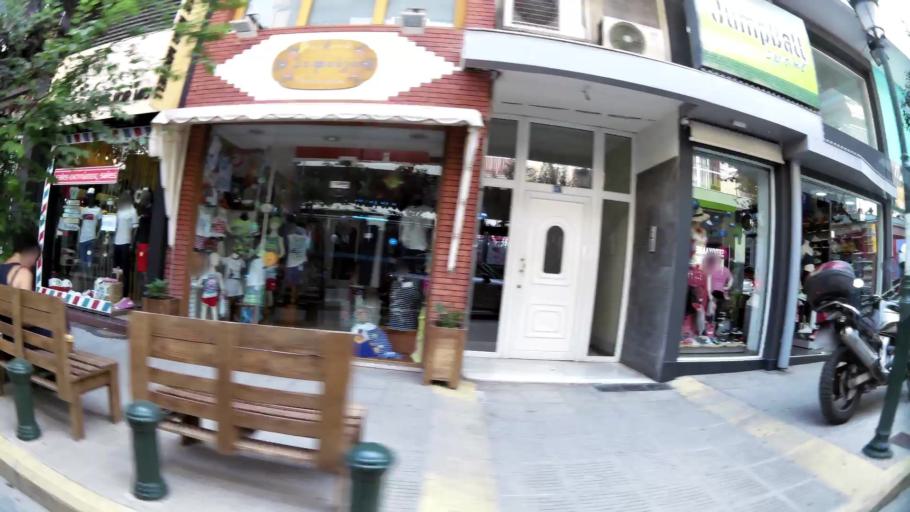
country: GR
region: Central Macedonia
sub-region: Nomos Thessalonikis
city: Polichni
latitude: 40.6624
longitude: 22.9480
